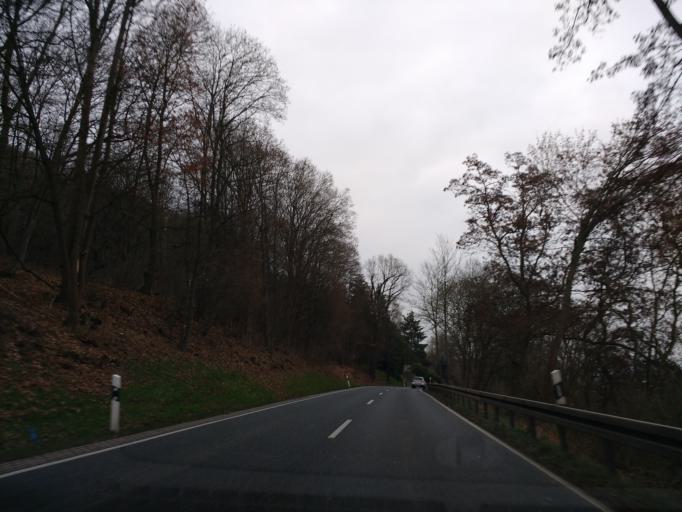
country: DE
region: Hesse
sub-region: Regierungsbezirk Kassel
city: Rotenburg an der Fulda
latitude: 51.0075
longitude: 9.7156
